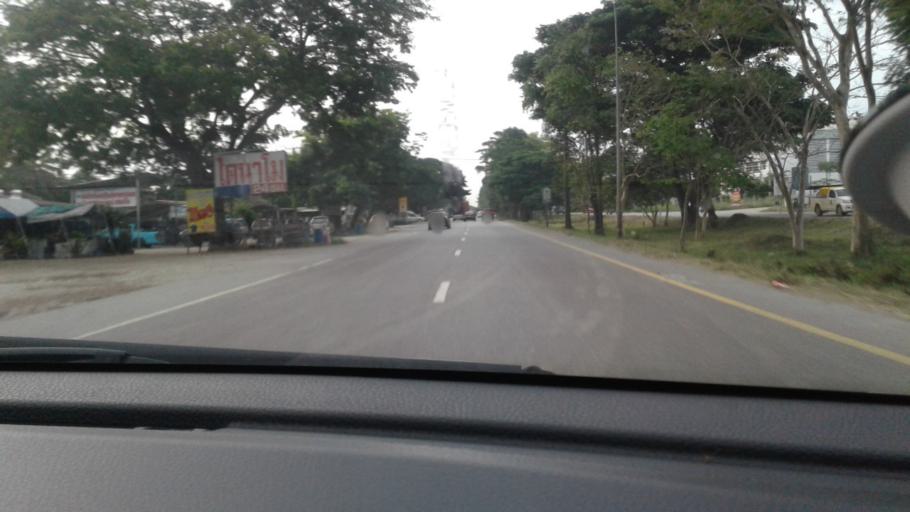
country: TH
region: Prachuap Khiri Khan
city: Pran Buri
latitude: 12.4217
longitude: 99.9229
